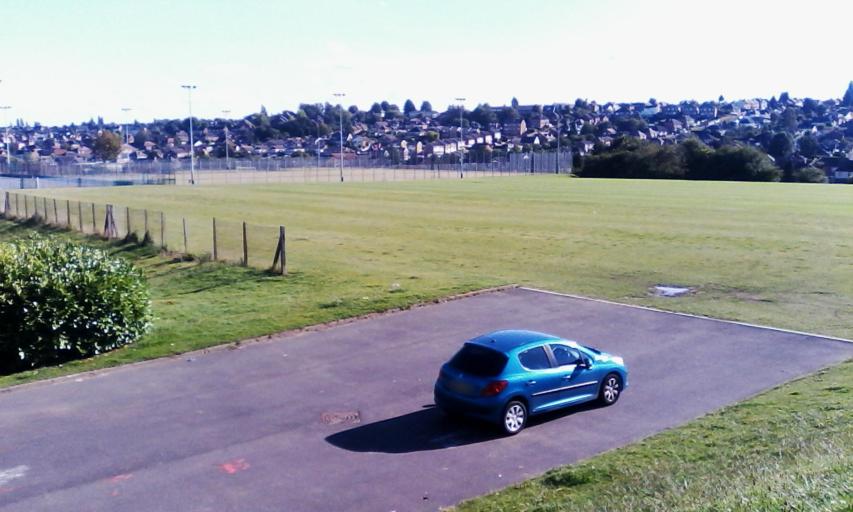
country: GB
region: England
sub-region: Nottinghamshire
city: Arnold
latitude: 52.9749
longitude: -1.1059
